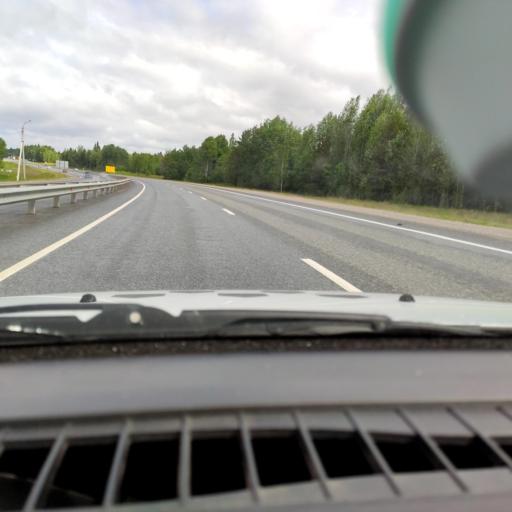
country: RU
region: Perm
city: Polazna
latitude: 58.2345
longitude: 56.4257
